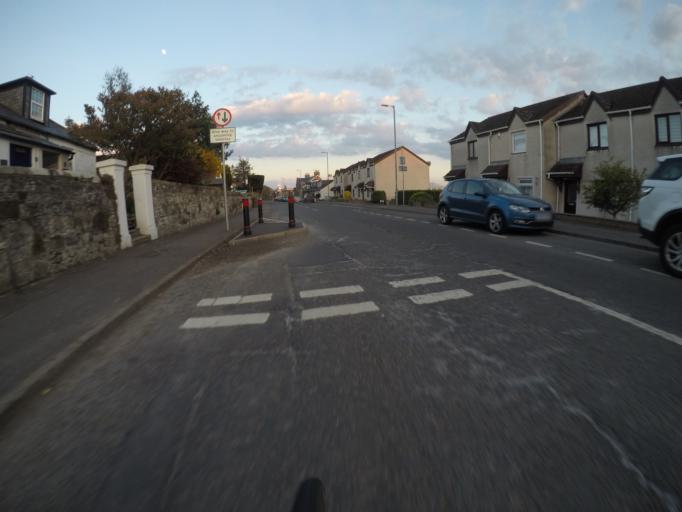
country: GB
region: Scotland
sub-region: South Ayrshire
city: Troon
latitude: 55.5513
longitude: -4.6251
